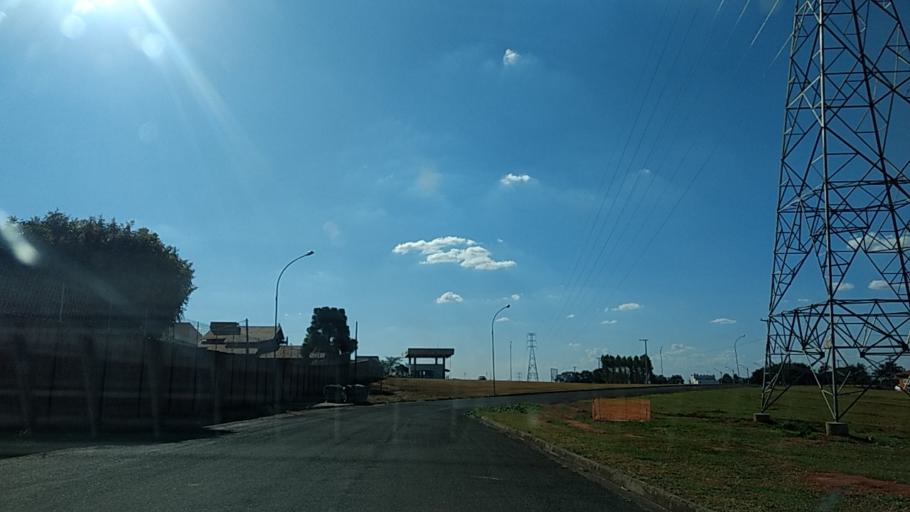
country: BR
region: Sao Paulo
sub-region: Botucatu
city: Botucatu
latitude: -22.8521
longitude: -48.4350
